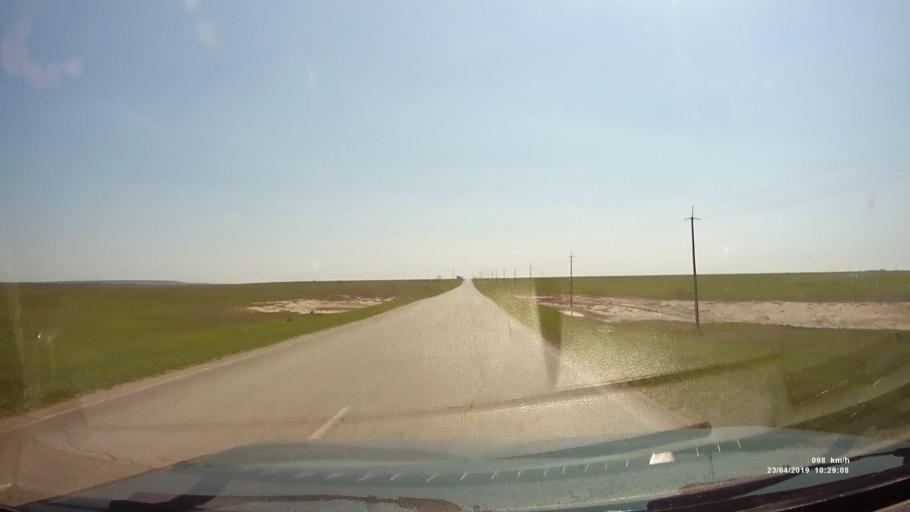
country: RU
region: Kalmykiya
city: Yashalta
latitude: 46.6006
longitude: 42.5207
